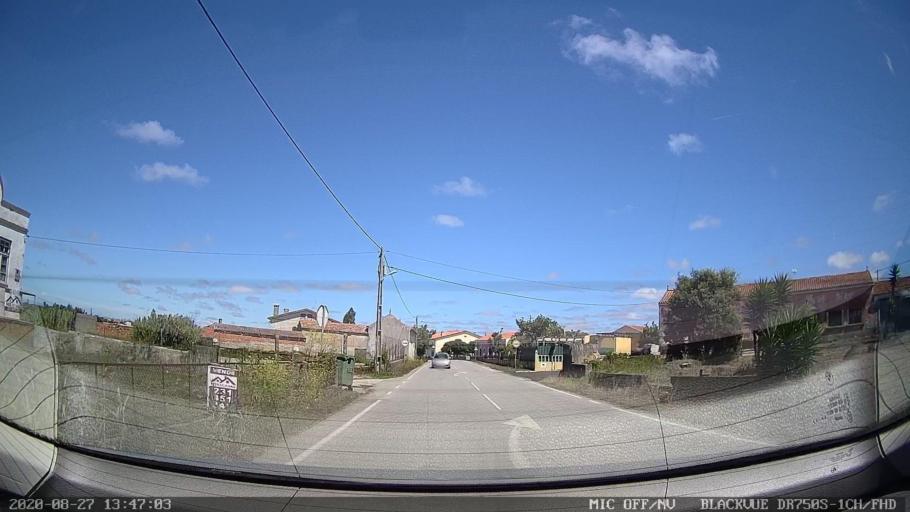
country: PT
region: Coimbra
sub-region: Mira
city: Mira
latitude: 40.3909
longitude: -8.7373
